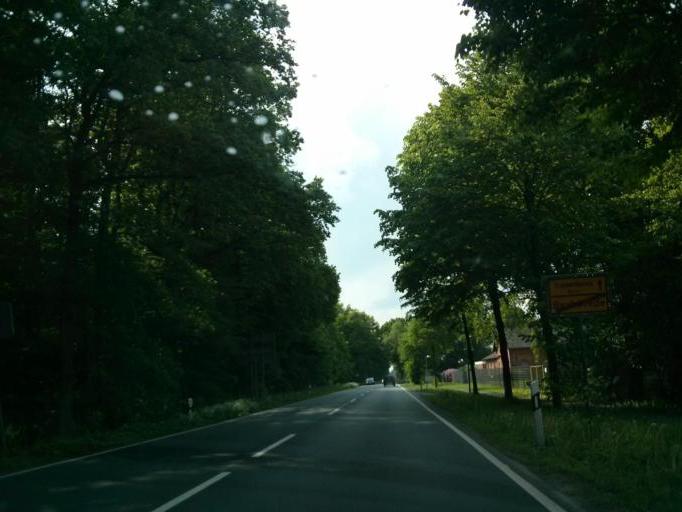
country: DE
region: Lower Saxony
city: Loxstedt
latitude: 53.4842
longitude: 8.6803
